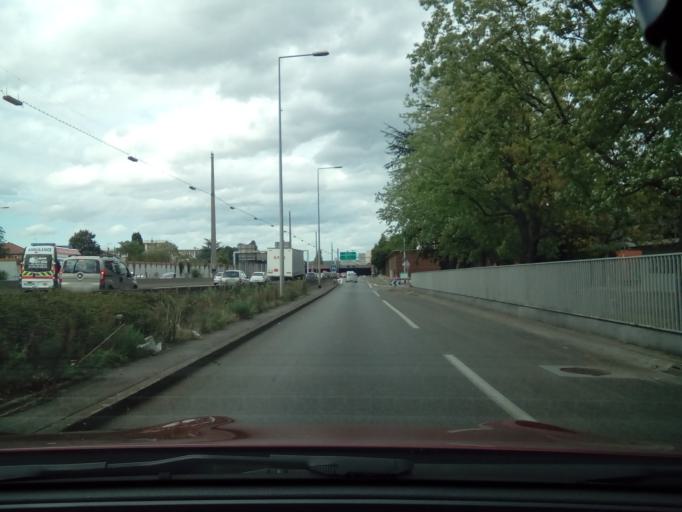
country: FR
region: Rhone-Alpes
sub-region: Departement du Rhone
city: Bron
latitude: 45.7528
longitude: 4.9082
